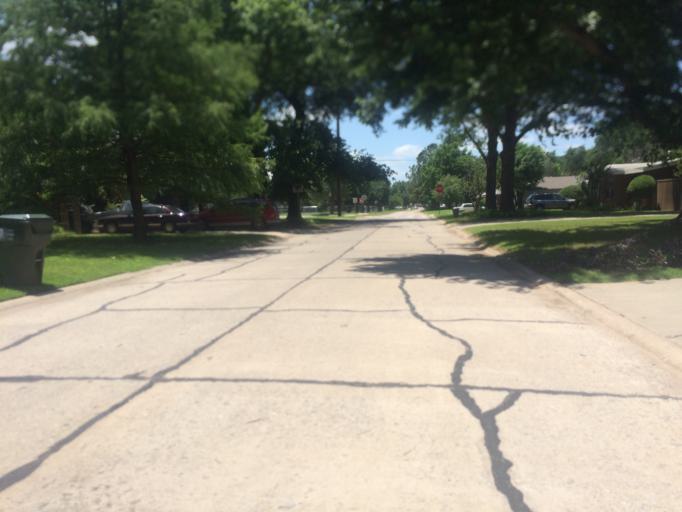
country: US
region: Oklahoma
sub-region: Cleveland County
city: Norman
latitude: 35.2143
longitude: -97.4626
